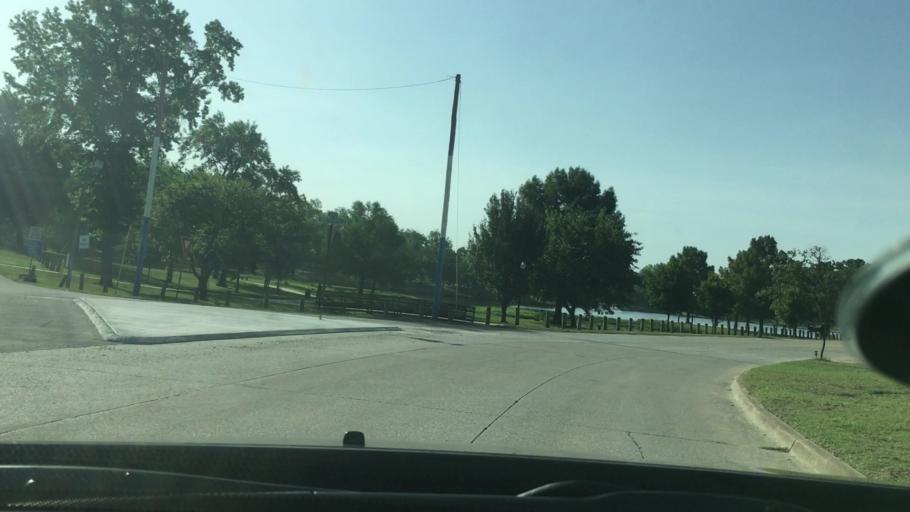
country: US
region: Oklahoma
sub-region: Pontotoc County
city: Ada
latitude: 34.7662
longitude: -96.6568
